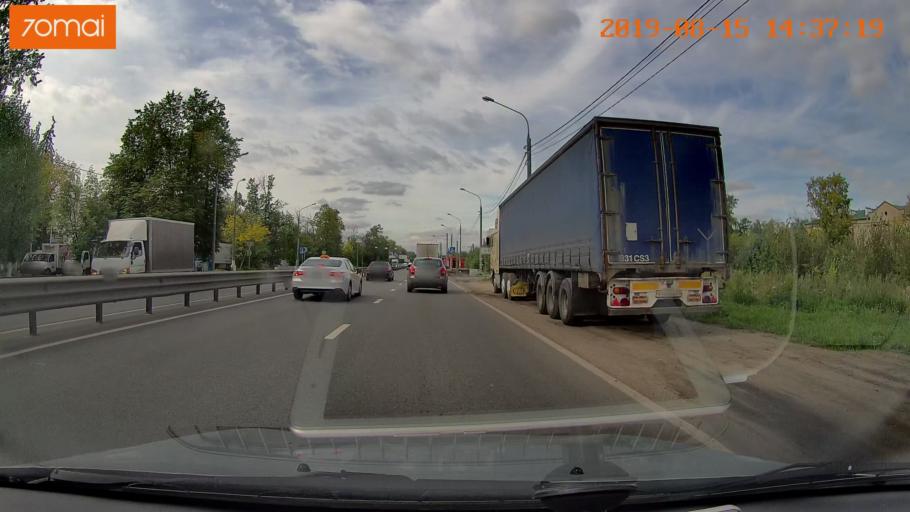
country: RU
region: Moskovskaya
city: Tomilino
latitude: 55.6519
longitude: 37.9280
